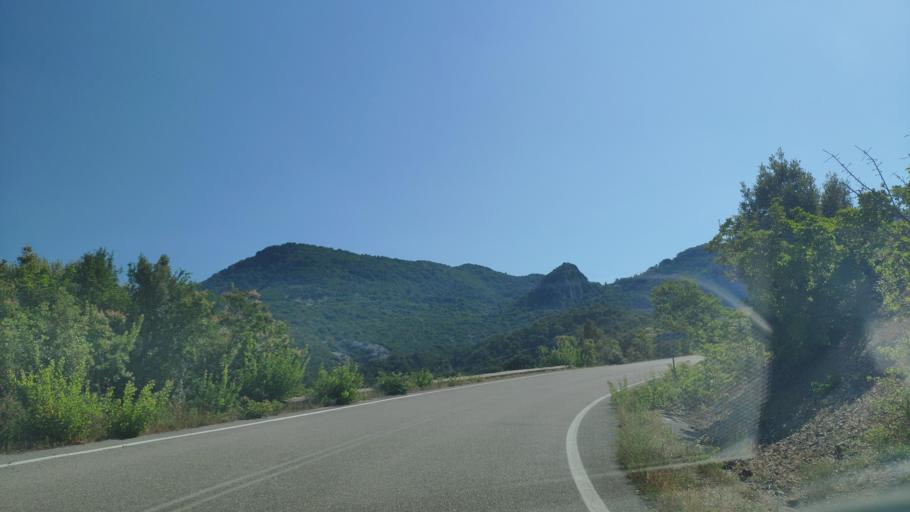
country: GR
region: West Greece
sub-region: Nomos Aitolias kai Akarnanias
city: Sardinia
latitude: 38.9216
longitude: 21.3942
